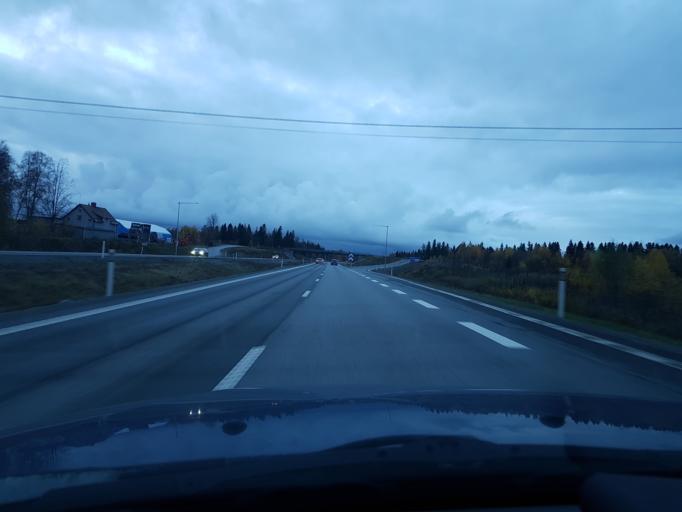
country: SE
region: Vaesterbotten
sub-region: Skelleftea Kommun
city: Kage
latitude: 64.8265
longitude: 21.0211
